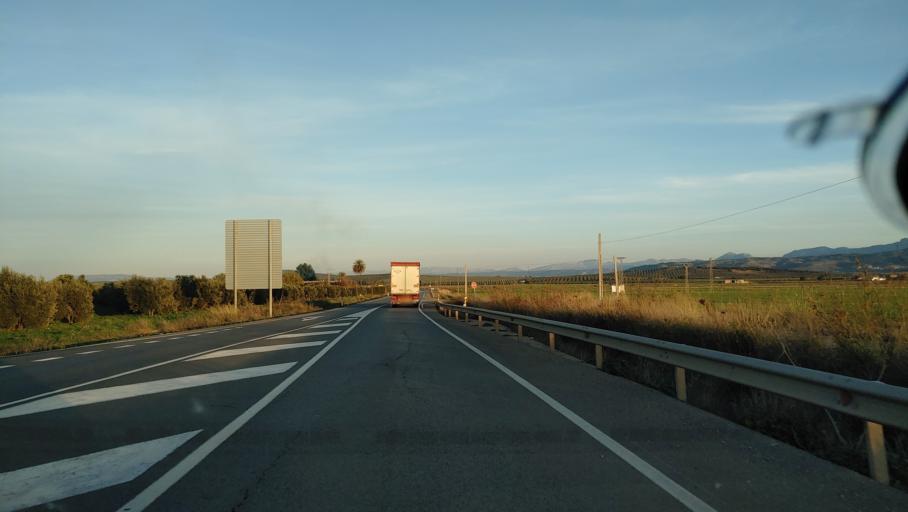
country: ES
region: Andalusia
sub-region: Provincia de Malaga
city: Humilladero
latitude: 37.0619
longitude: -4.7157
